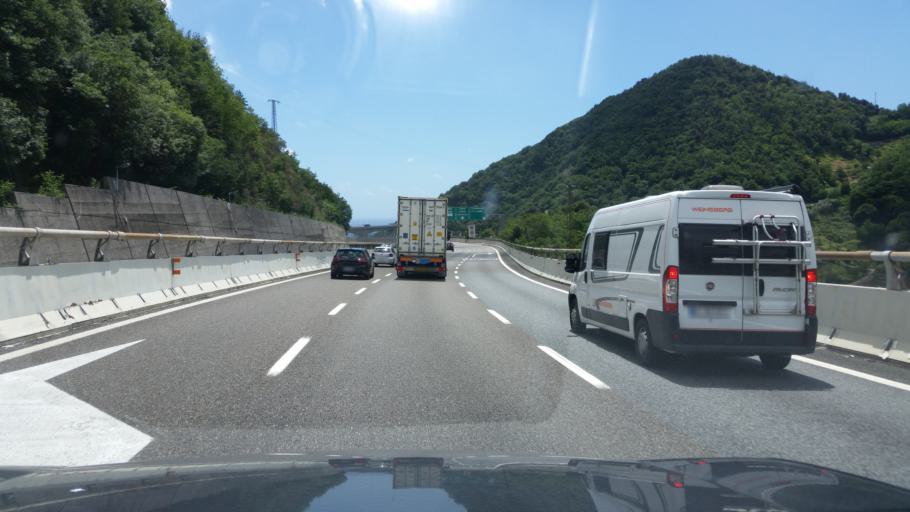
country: IT
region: Liguria
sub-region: Provincia di Genova
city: Mele
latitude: 44.4373
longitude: 8.7374
